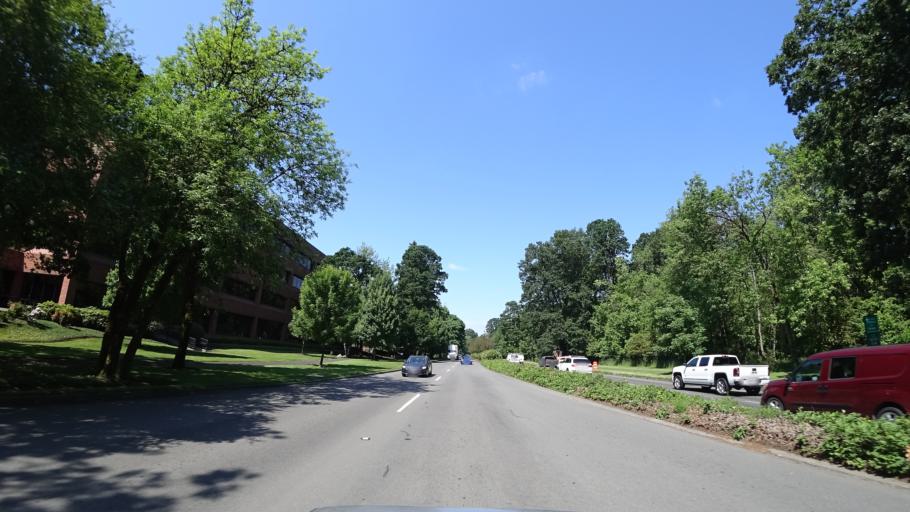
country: US
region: Oregon
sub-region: Washington County
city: Durham
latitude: 45.4189
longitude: -122.7330
